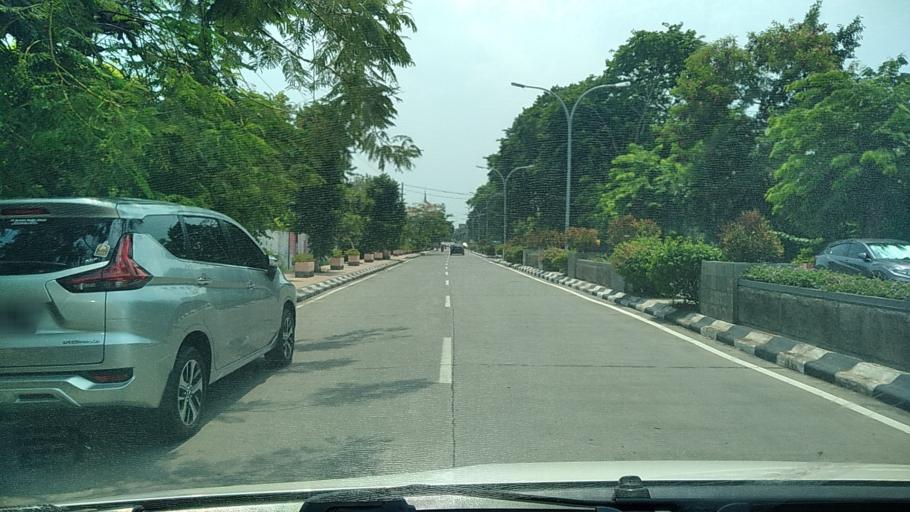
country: ID
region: Central Java
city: Semarang
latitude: -6.9844
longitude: 110.3709
